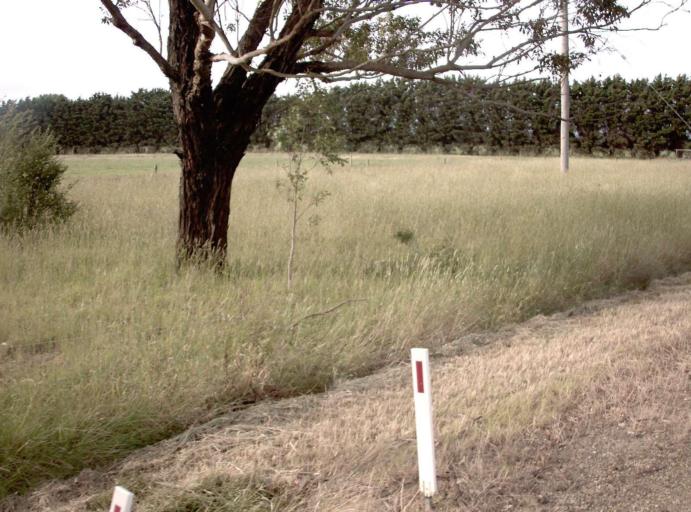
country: AU
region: Victoria
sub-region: Wellington
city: Heyfield
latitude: -38.0119
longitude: 146.7762
